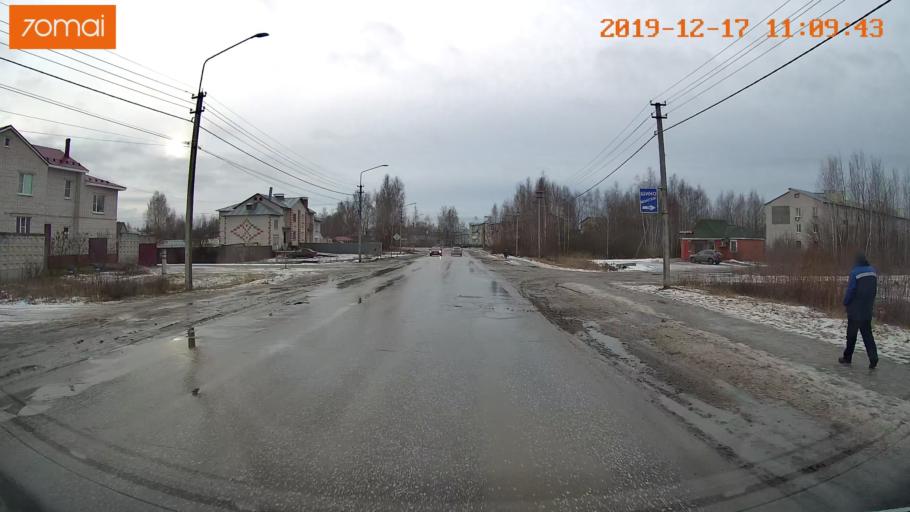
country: RU
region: Vladimir
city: Gus'-Khrustal'nyy
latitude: 55.5985
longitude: 40.6419
